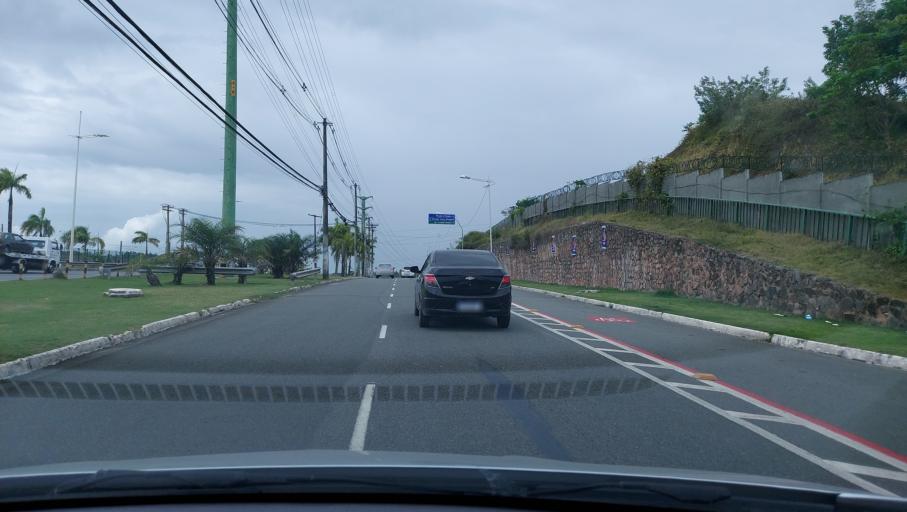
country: BR
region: Bahia
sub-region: Lauro De Freitas
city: Lauro de Freitas
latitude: -12.9294
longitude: -38.3873
